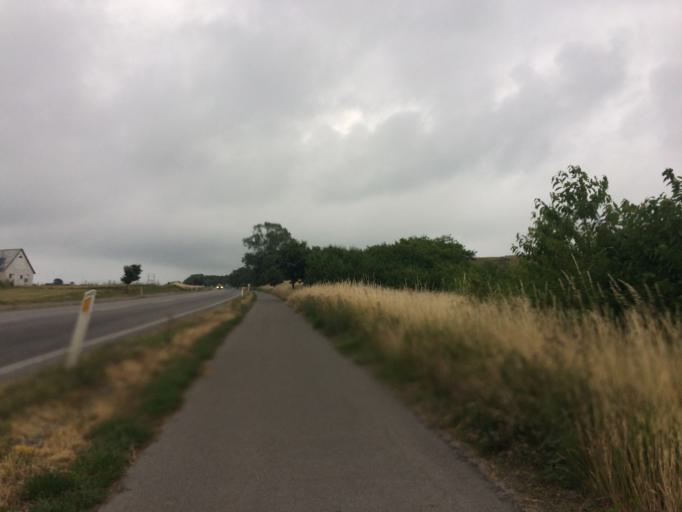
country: DK
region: Capital Region
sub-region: Bornholm Kommune
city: Ronne
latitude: 55.1038
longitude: 14.7294
